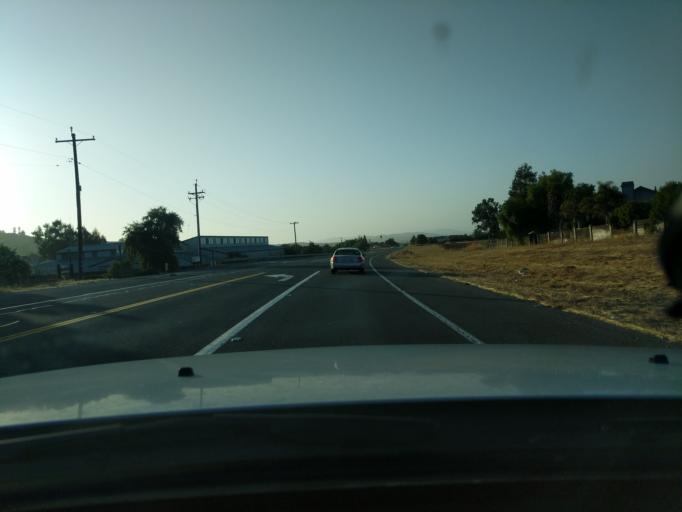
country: US
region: California
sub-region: San Benito County
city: Ridgemark
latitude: 36.8172
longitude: -121.3664
